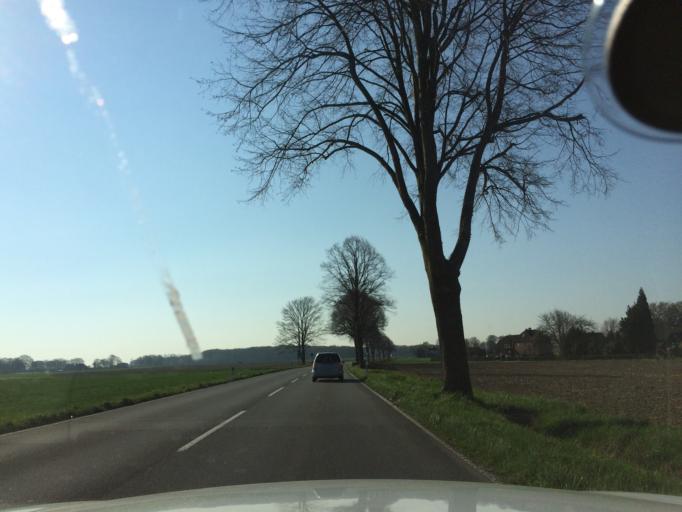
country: DE
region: North Rhine-Westphalia
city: Marl
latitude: 51.6337
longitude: 7.0842
